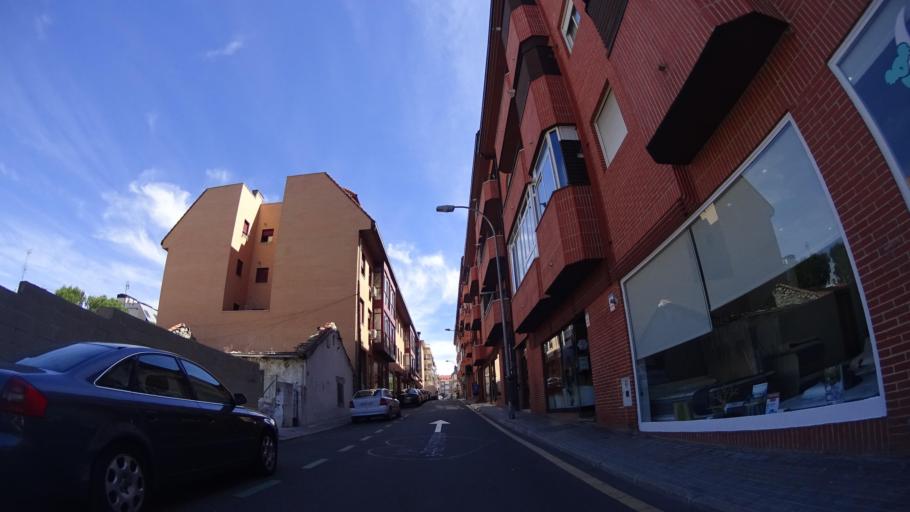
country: ES
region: Madrid
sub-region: Provincia de Madrid
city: Collado-Villalba
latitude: 40.6284
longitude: -4.0056
